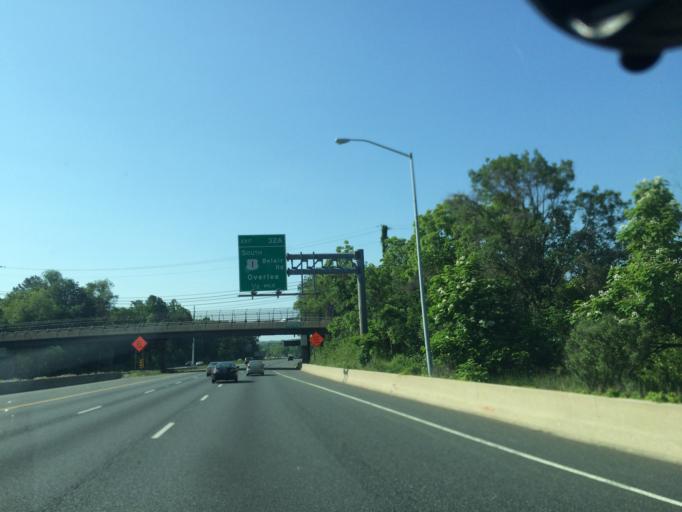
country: US
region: Maryland
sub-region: Baltimore County
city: Carney
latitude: 39.3806
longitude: -76.5206
